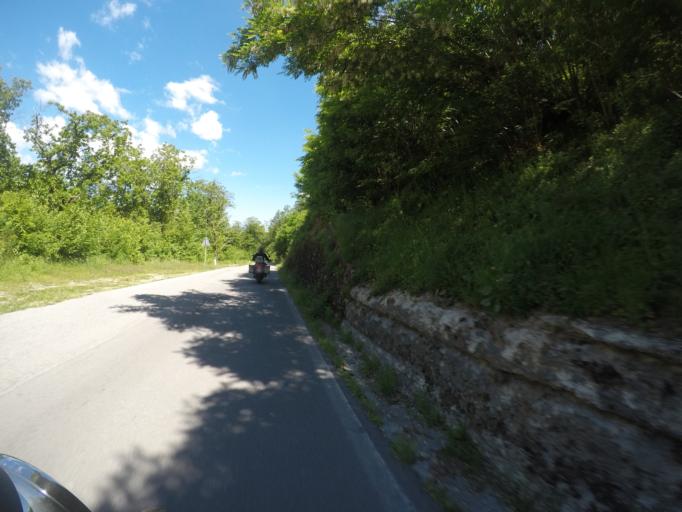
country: IT
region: Tuscany
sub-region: Provincia di Lucca
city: Careggine
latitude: 44.1273
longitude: 10.3362
